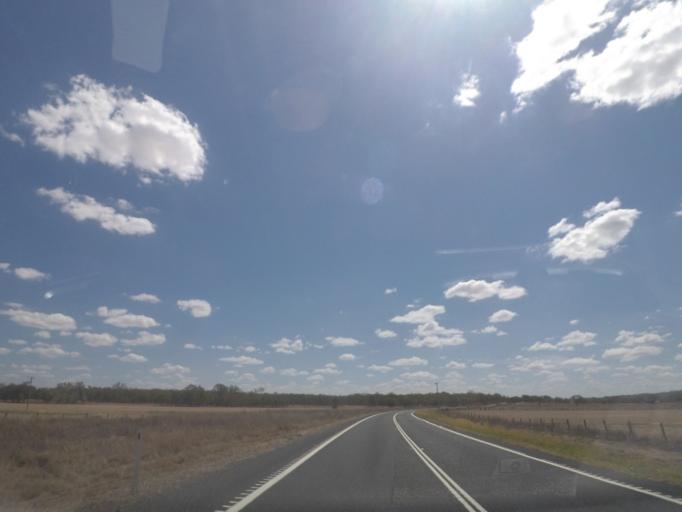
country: AU
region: Queensland
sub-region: Southern Downs
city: Warwick
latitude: -28.1835
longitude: 151.8161
